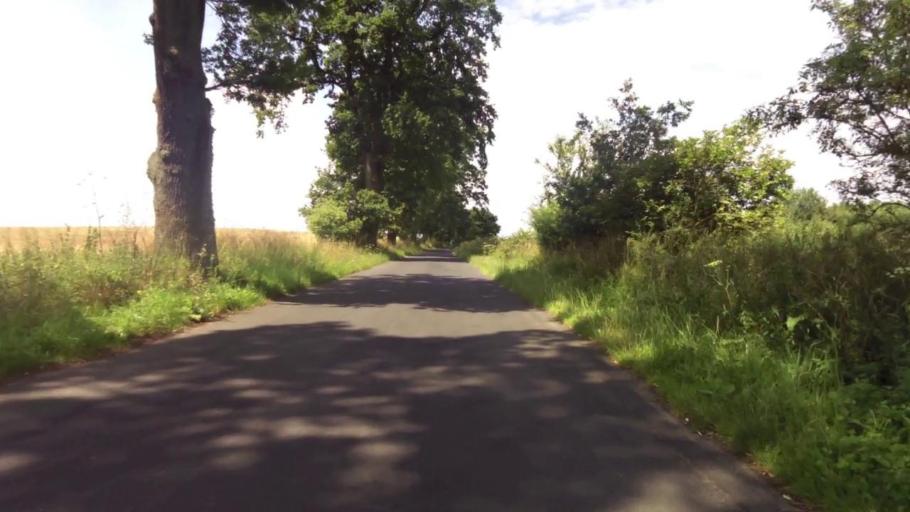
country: PL
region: West Pomeranian Voivodeship
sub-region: Powiat stargardzki
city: Dobrzany
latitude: 53.4275
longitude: 15.4651
